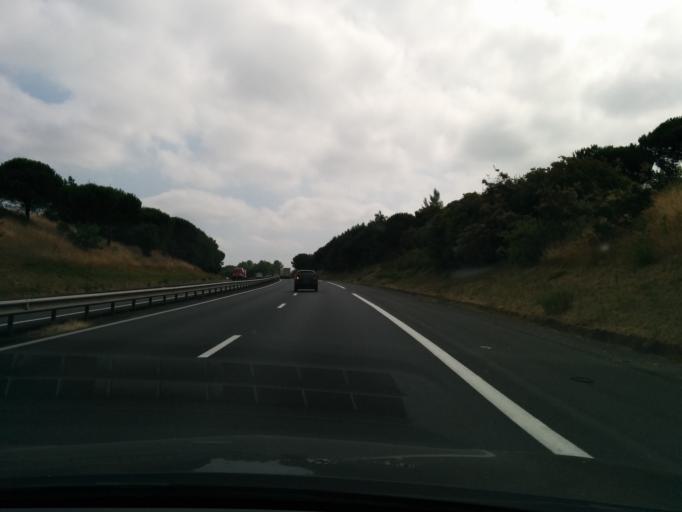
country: FR
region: Midi-Pyrenees
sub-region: Departement de la Haute-Garonne
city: Beaupuy
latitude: 43.6553
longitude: 1.5401
